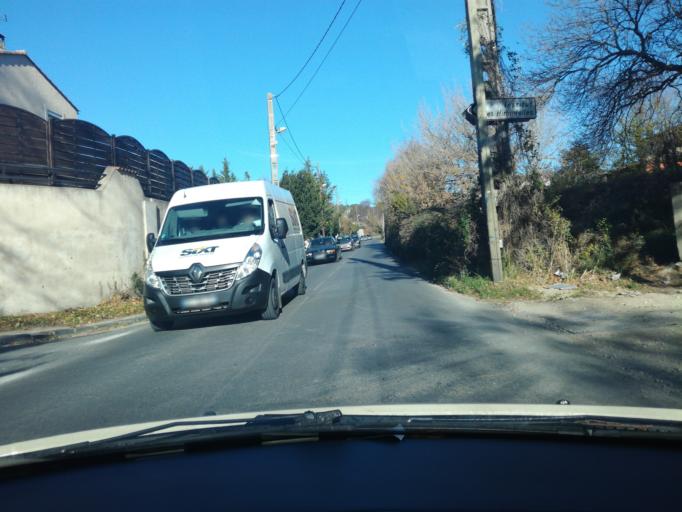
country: FR
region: Provence-Alpes-Cote d'Azur
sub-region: Departement des Bouches-du-Rhone
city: La Penne-sur-Huveaune
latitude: 43.3021
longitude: 5.5012
